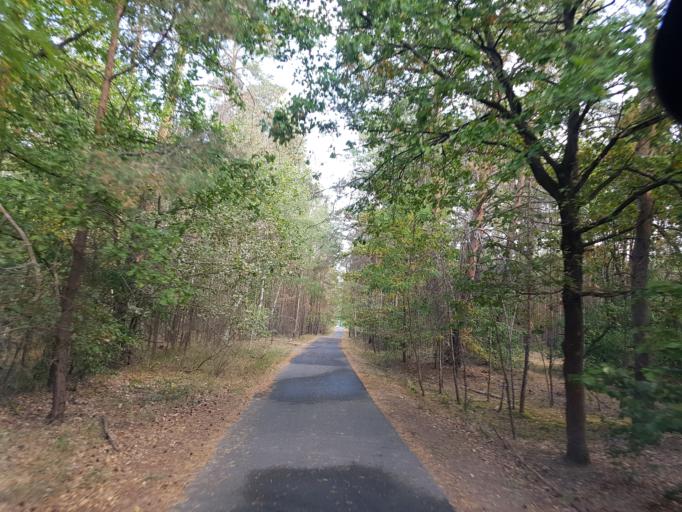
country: DE
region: Brandenburg
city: Finsterwalde
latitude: 51.6012
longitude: 13.7599
